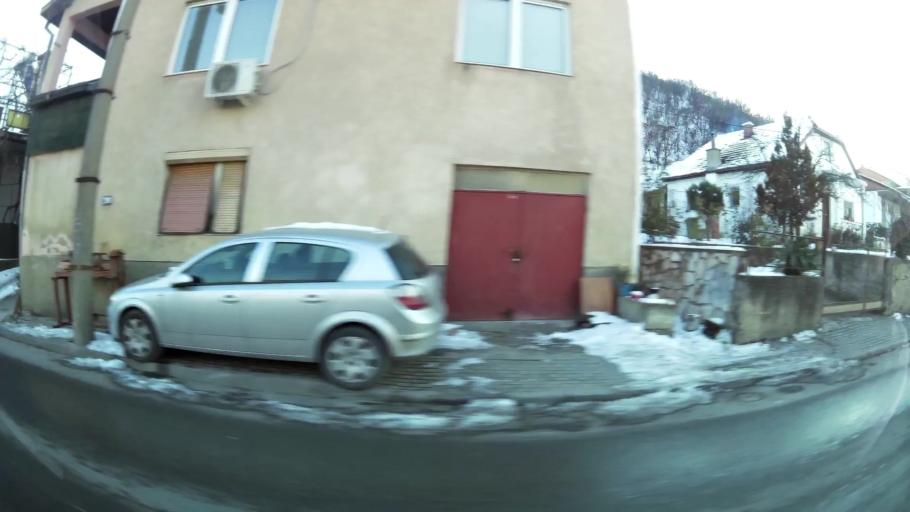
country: MK
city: Krushopek
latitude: 41.9986
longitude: 21.3820
